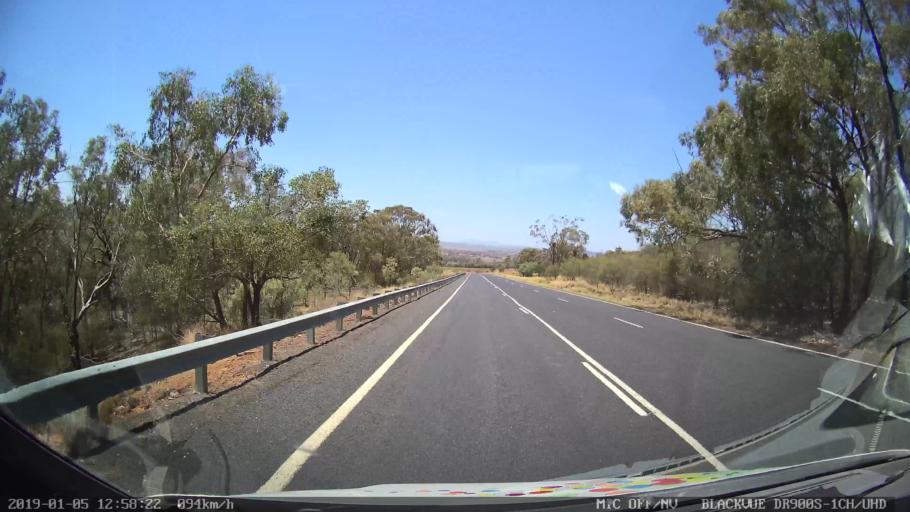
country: AU
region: New South Wales
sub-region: Warrumbungle Shire
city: Coonabarabran
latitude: -31.1122
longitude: 149.7485
